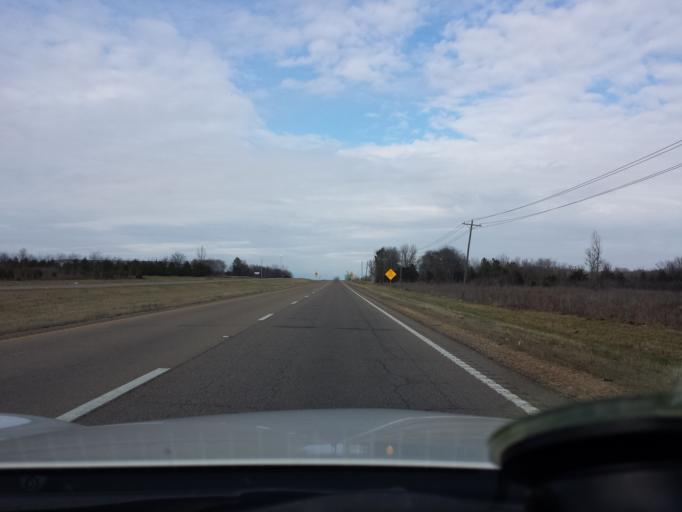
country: US
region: Mississippi
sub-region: Clay County
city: West Point
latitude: 33.5239
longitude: -88.6588
